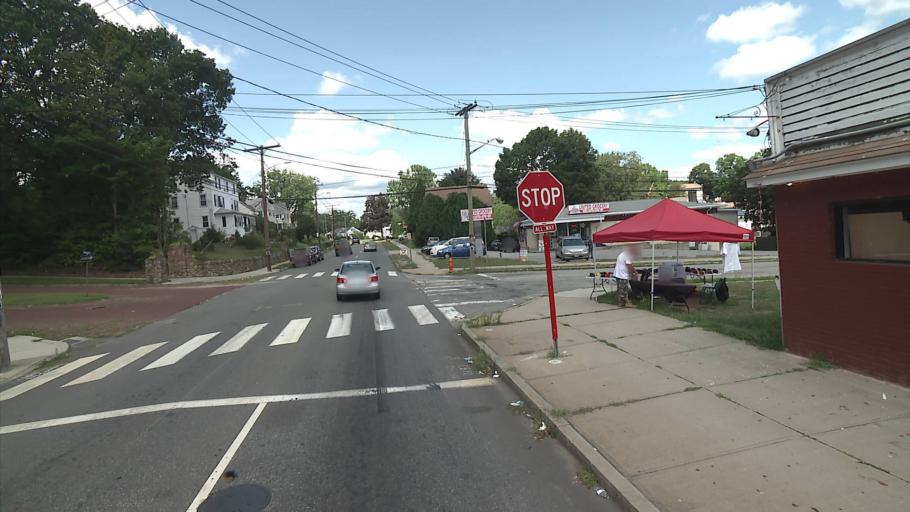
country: US
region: Connecticut
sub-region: New London County
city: New London
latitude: 41.3557
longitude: -72.1117
